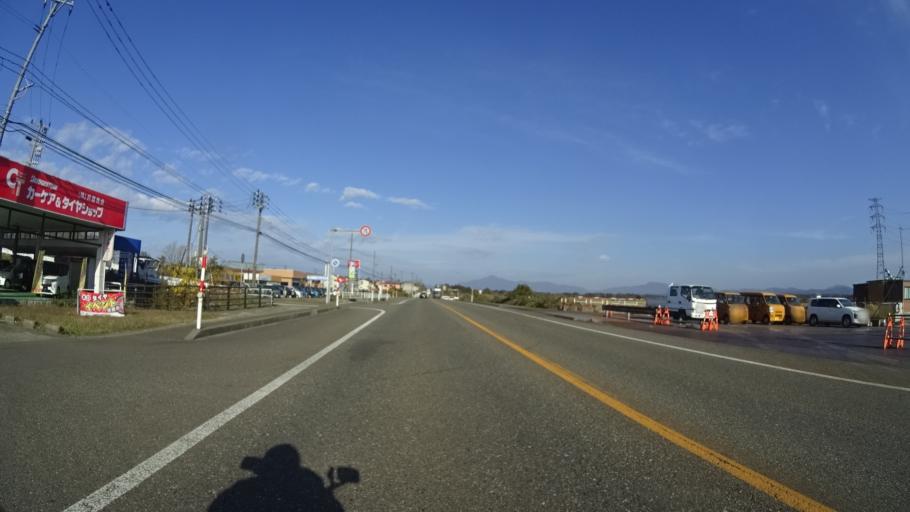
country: JP
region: Niigata
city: Joetsu
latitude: 37.1961
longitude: 138.2855
